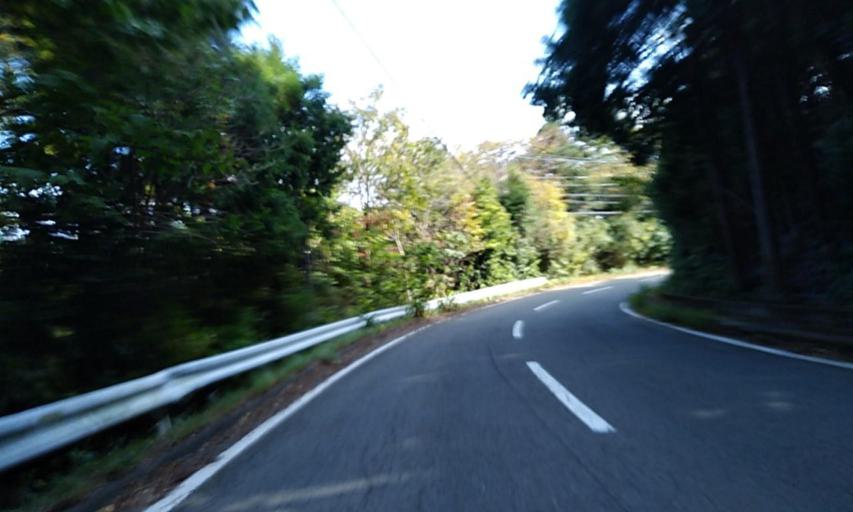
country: JP
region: Wakayama
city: Gobo
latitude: 33.9670
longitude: 135.0968
